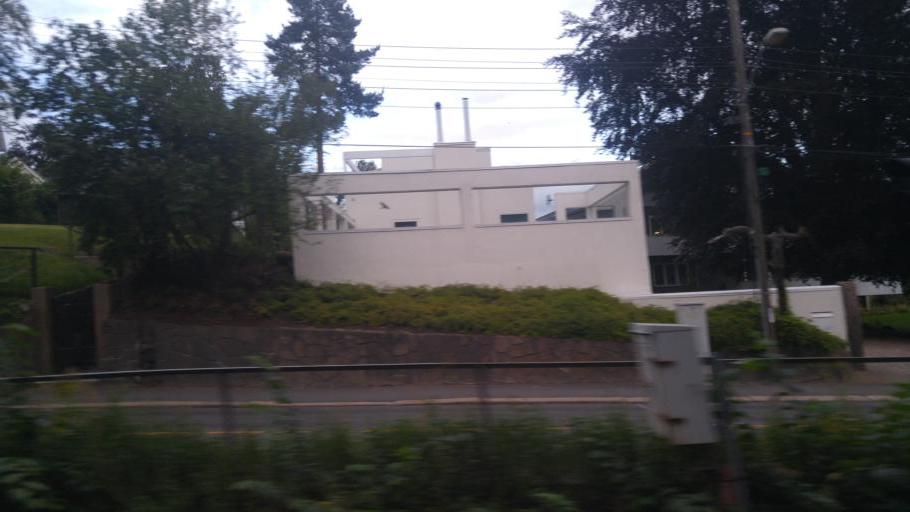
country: NO
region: Oslo
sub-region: Oslo
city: Sjolyststranda
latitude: 59.9381
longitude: 10.7054
